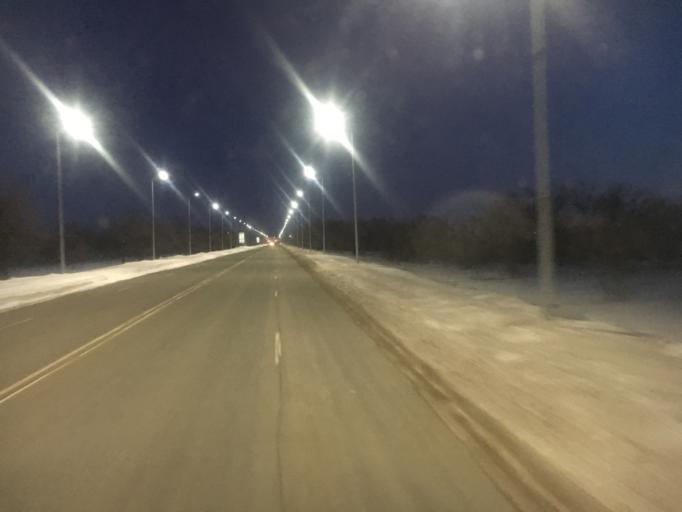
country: KZ
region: Batys Qazaqstan
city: Oral
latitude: 51.1602
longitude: 51.5302
